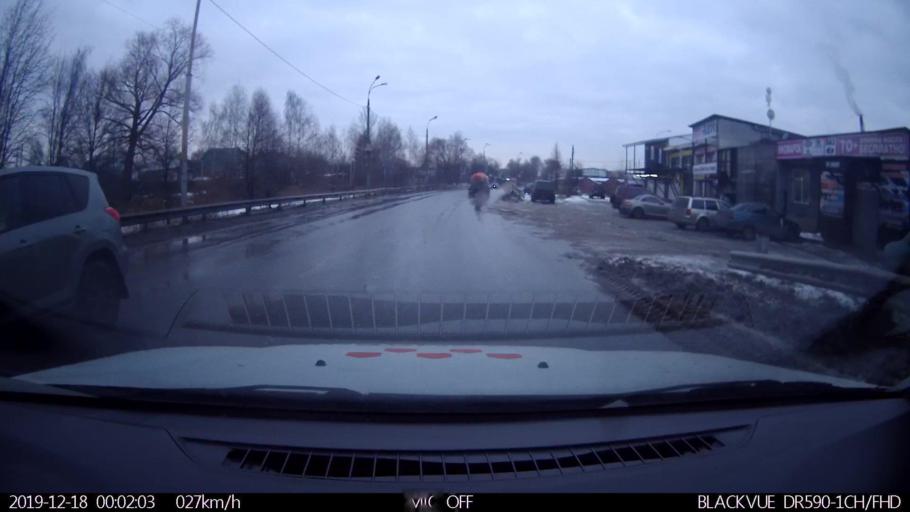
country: RU
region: Nizjnij Novgorod
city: Gorbatovka
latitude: 56.3707
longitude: 43.8251
